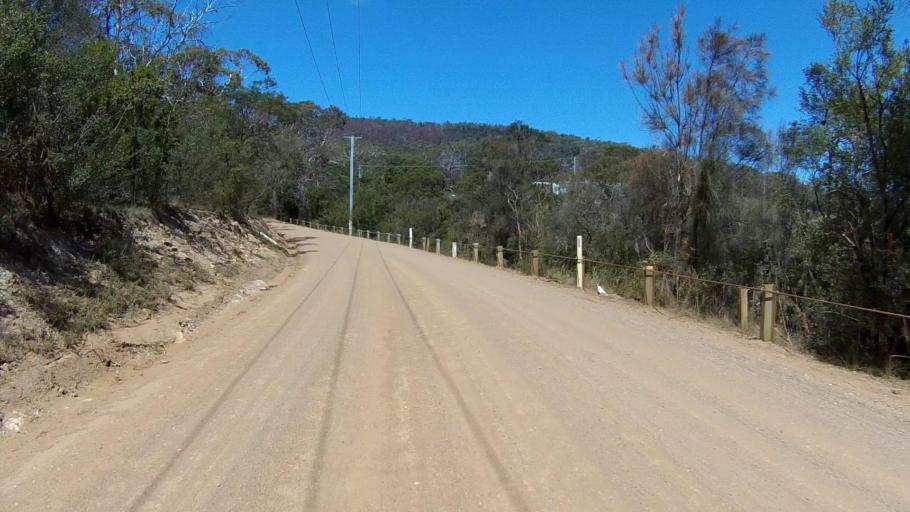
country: AU
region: Tasmania
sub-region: Clarence
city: Lauderdale
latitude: -42.9311
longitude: 147.4659
